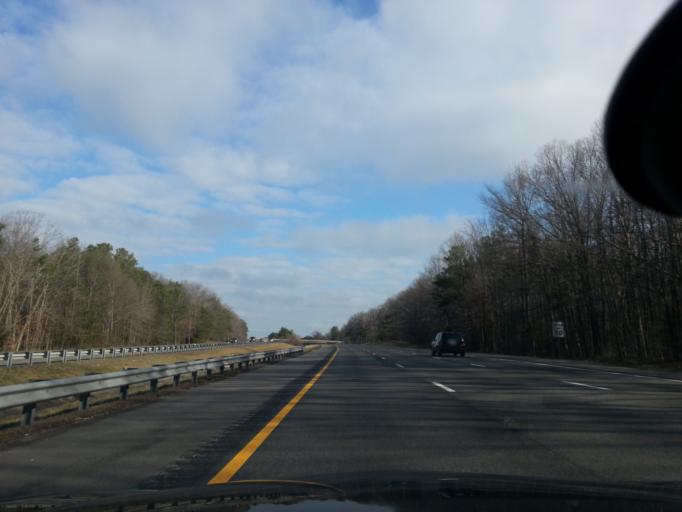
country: US
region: Virginia
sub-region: Caroline County
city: Bowling Green
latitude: 37.9887
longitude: -77.4926
